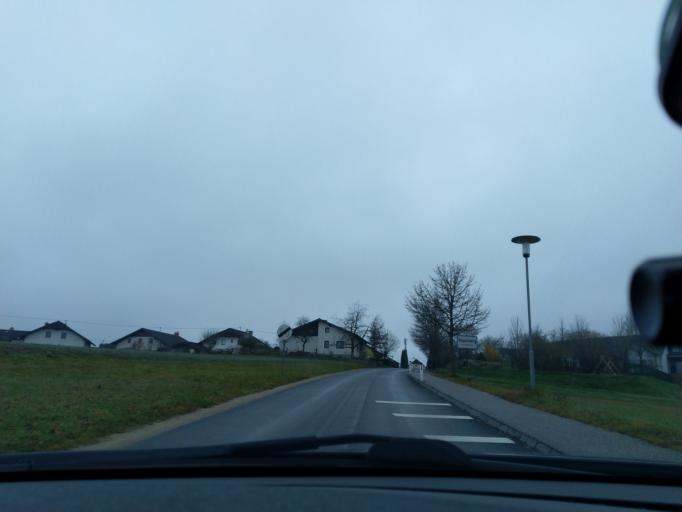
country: AT
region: Upper Austria
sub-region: Politischer Bezirk Urfahr-Umgebung
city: Engerwitzdorf
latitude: 48.3706
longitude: 14.5178
